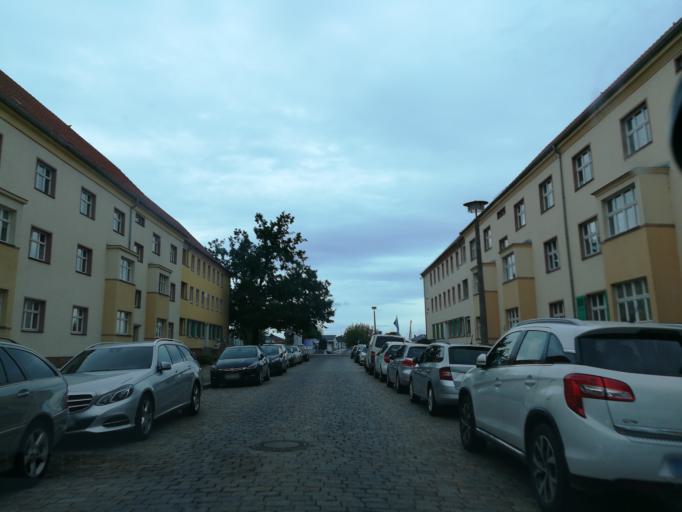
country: DE
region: Saxony-Anhalt
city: Magdeburg
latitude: 52.1394
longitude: 11.6185
